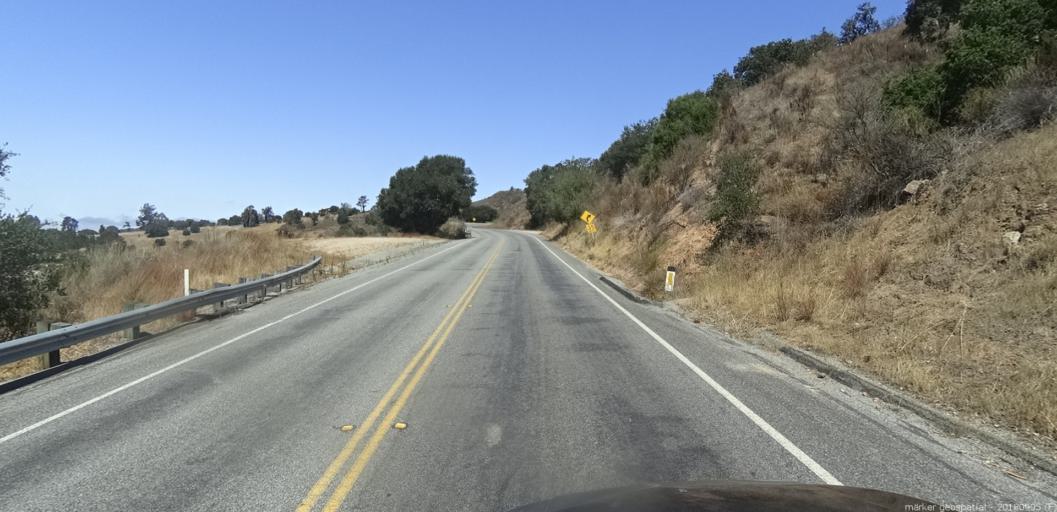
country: US
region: California
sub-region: Monterey County
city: Carmel Valley Village
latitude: 36.5120
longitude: -121.7551
